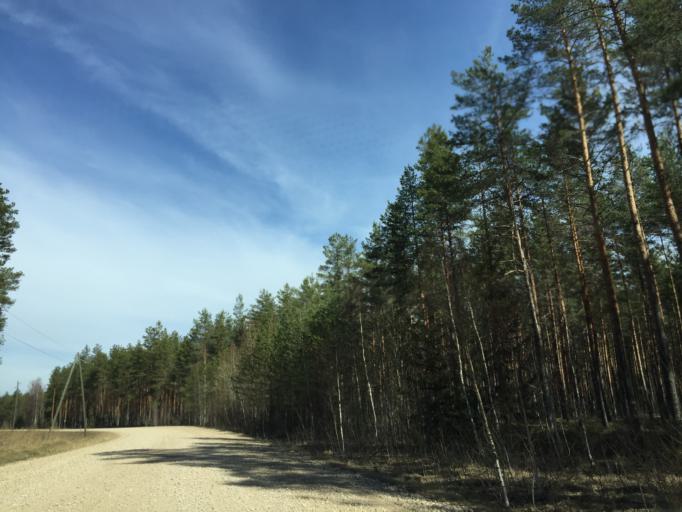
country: LV
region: Strenci
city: Seda
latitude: 57.6439
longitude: 25.8633
